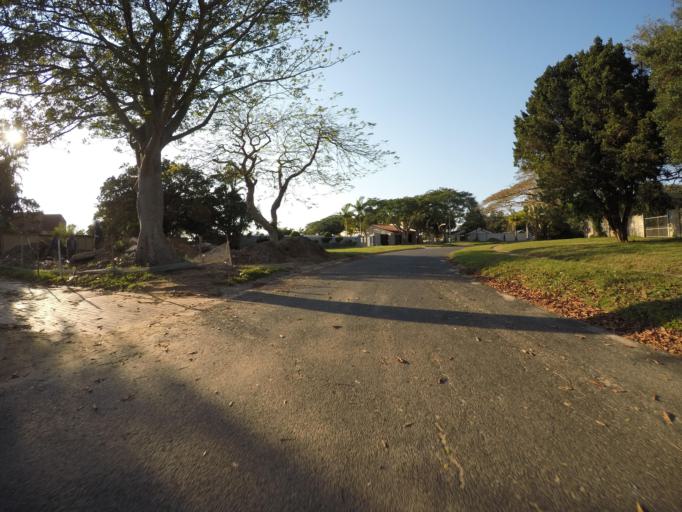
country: ZA
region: KwaZulu-Natal
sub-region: uThungulu District Municipality
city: Richards Bay
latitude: -28.7725
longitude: 32.1058
